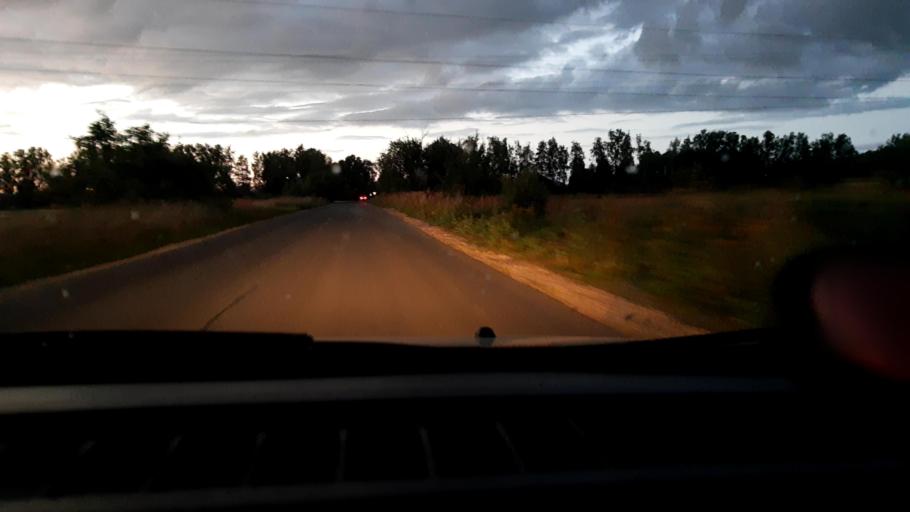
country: RU
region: Nizjnij Novgorod
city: Nizhniy Novgorod
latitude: 56.2095
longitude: 43.9704
